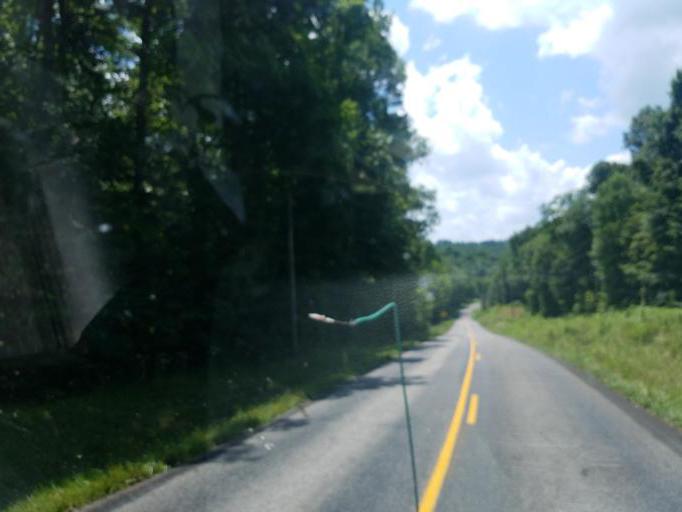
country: US
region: Kentucky
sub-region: Grayson County
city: Leitchfield
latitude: 37.5098
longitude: -86.4723
